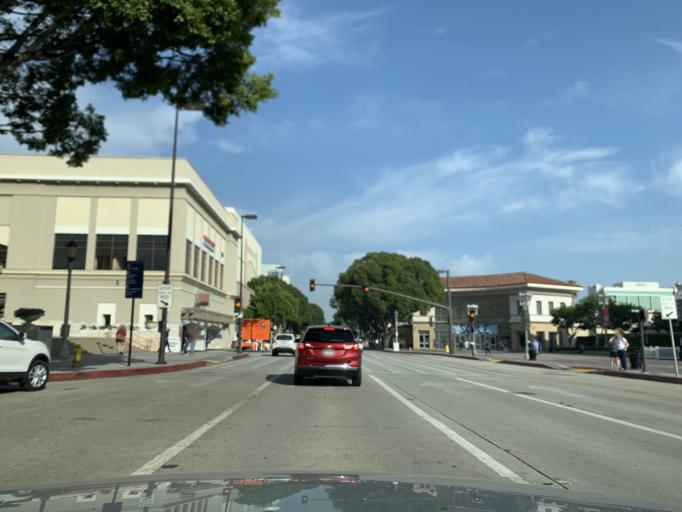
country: US
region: California
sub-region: Los Angeles County
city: Pasadena
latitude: 34.1446
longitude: -118.1445
